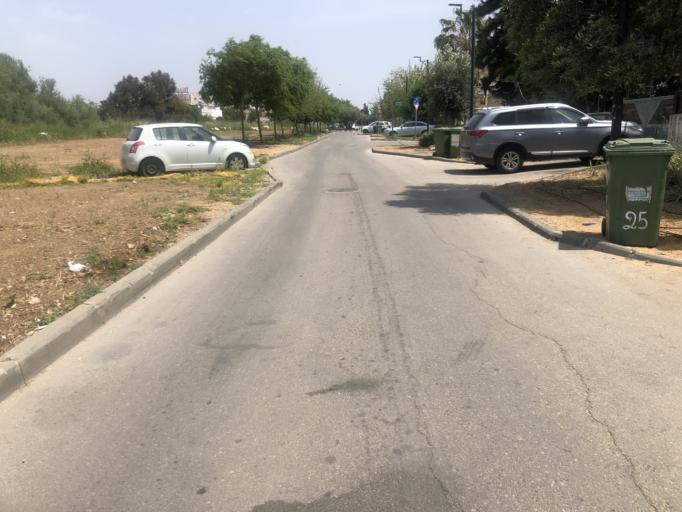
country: IL
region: Central District
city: Rosh Ha'Ayin
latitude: 32.0998
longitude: 34.9379
